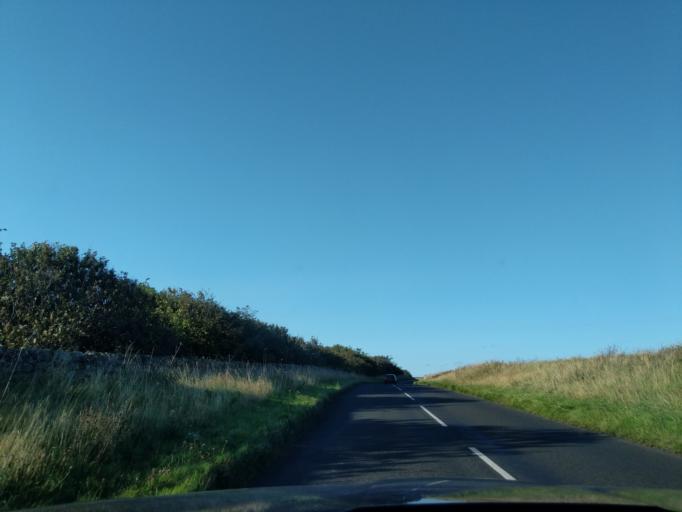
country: GB
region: England
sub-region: Northumberland
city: Lynemouth
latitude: 55.2205
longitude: -1.5303
